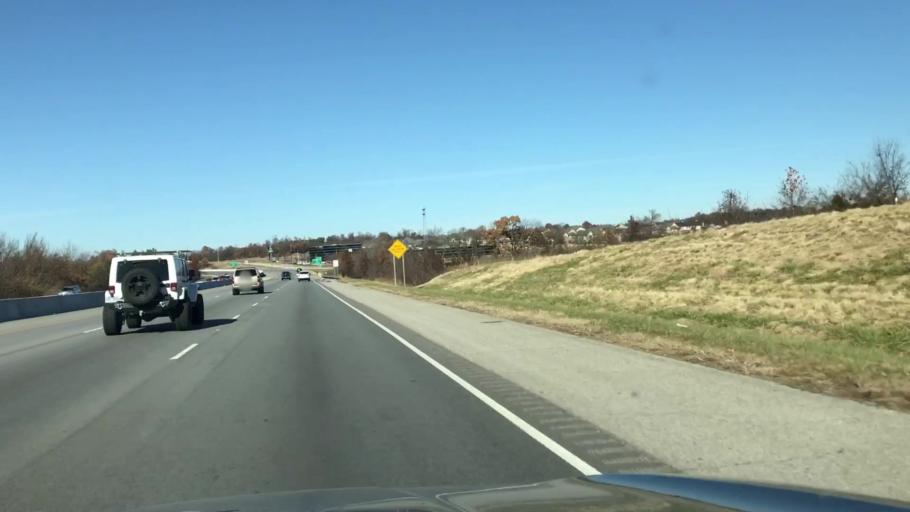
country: US
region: Arkansas
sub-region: Benton County
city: Lowell
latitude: 36.2901
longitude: -94.1616
